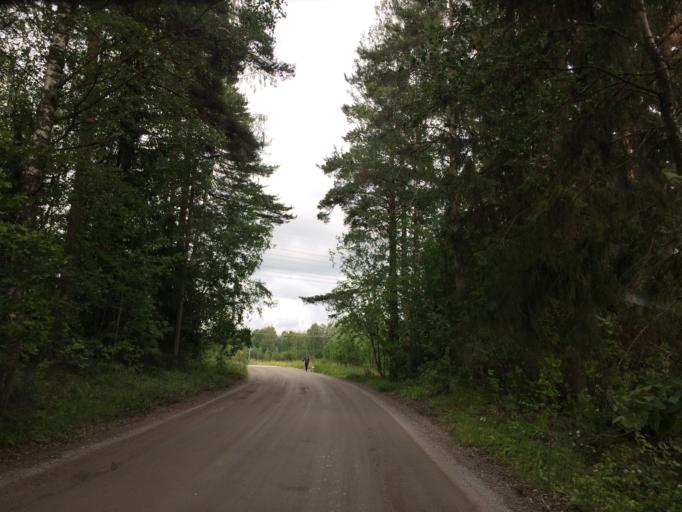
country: FI
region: Haeme
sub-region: Haemeenlinna
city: Haemeenlinna
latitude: 60.9670
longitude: 24.5311
